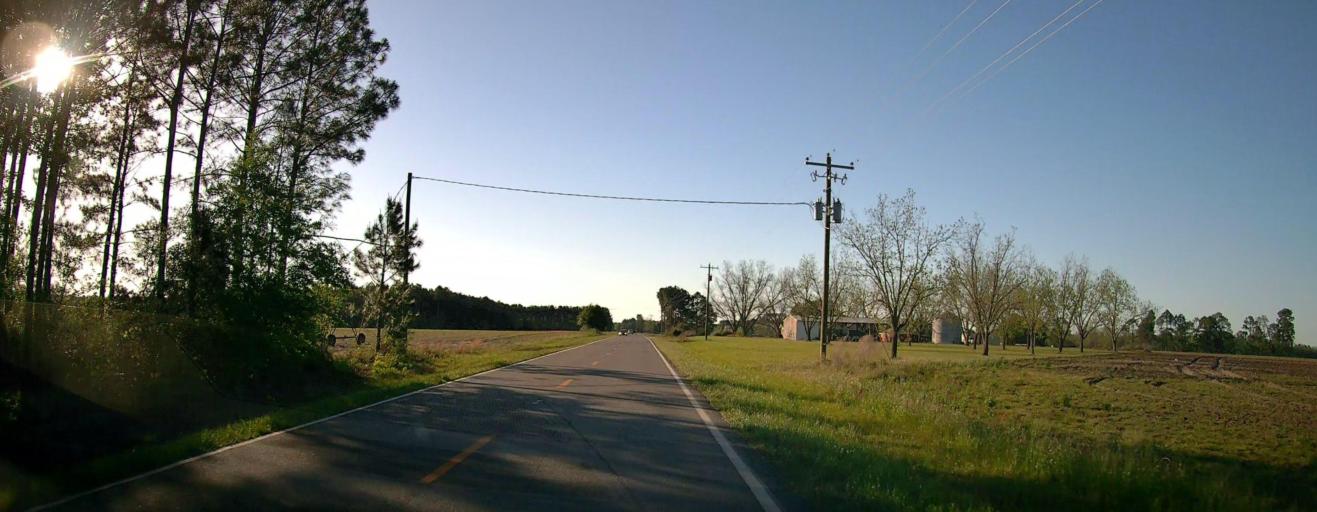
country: US
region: Georgia
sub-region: Ben Hill County
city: Fitzgerald
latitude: 31.6626
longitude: -83.1800
